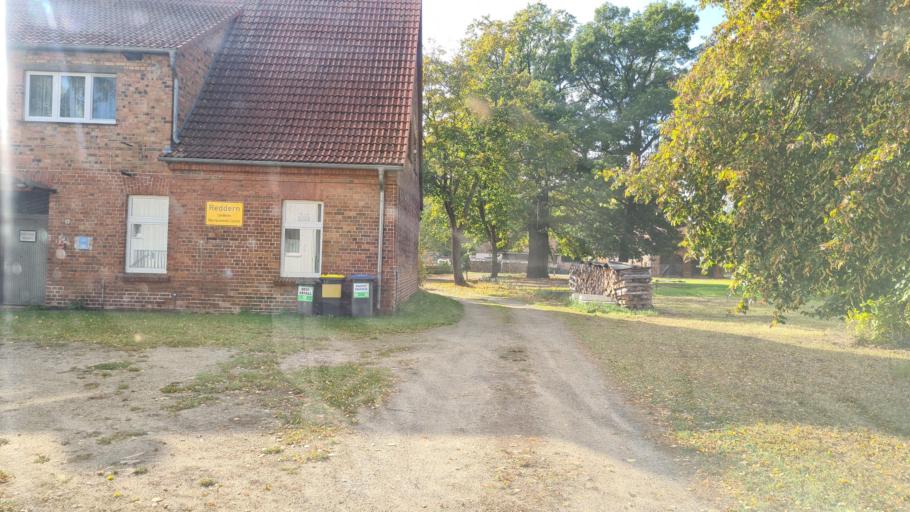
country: DE
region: Brandenburg
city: Altdobern
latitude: 51.6850
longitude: 14.0856
